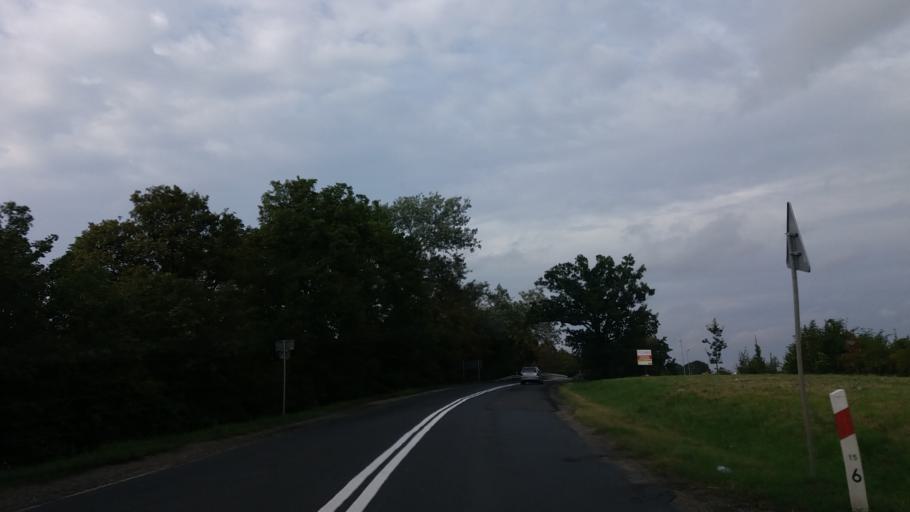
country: PL
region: Lower Silesian Voivodeship
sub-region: Powiat sredzki
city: Udanin
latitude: 51.0855
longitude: 16.4165
